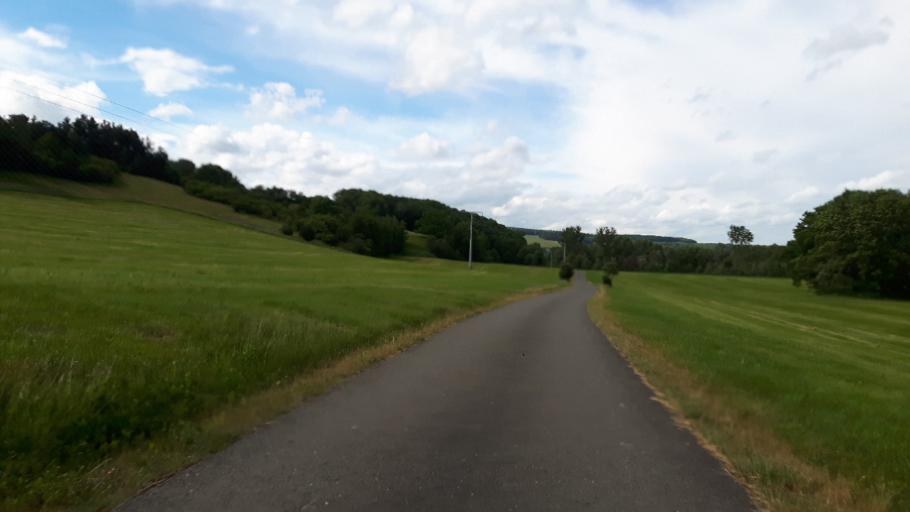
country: DE
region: Thuringia
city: Barchfeld
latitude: 50.8171
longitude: 11.1795
